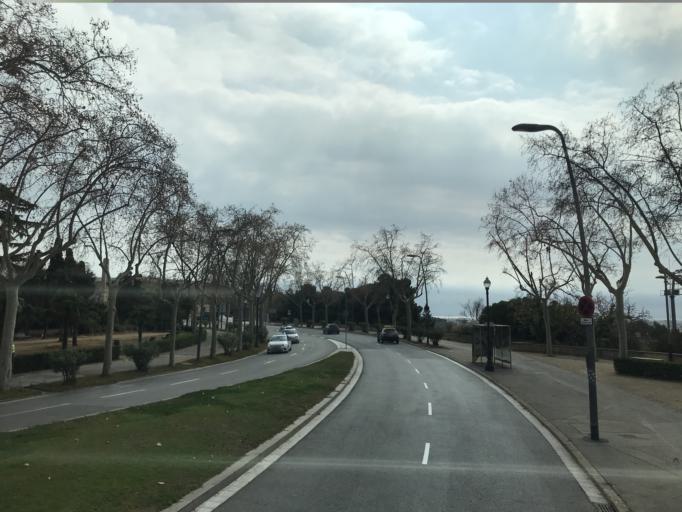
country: ES
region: Catalonia
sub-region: Provincia de Barcelona
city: Sants-Montjuic
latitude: 41.3667
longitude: 2.1447
